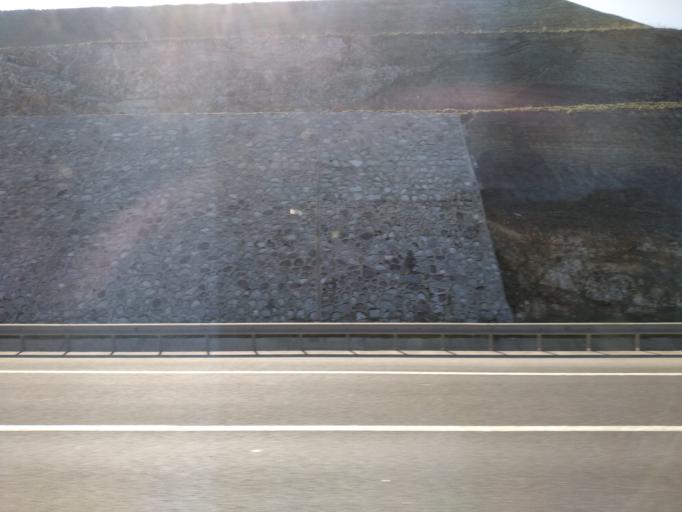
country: TR
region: Istanbul
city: Arikoey
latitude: 41.2261
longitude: 28.9822
